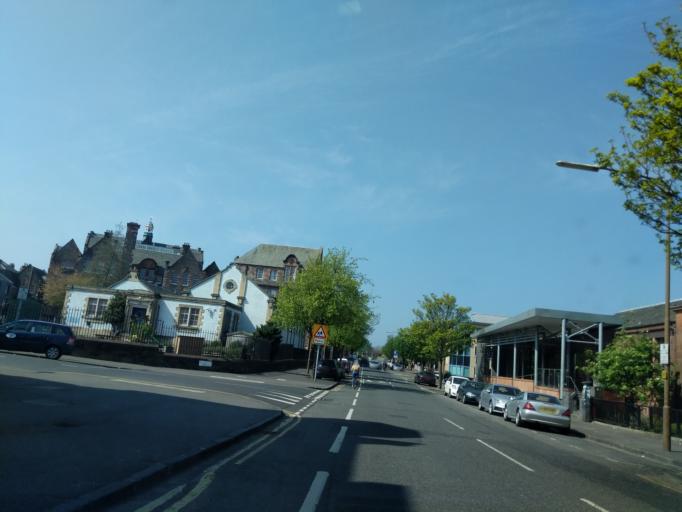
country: GB
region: Scotland
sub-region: Edinburgh
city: Edinburgh
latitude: 55.9649
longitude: -3.1869
